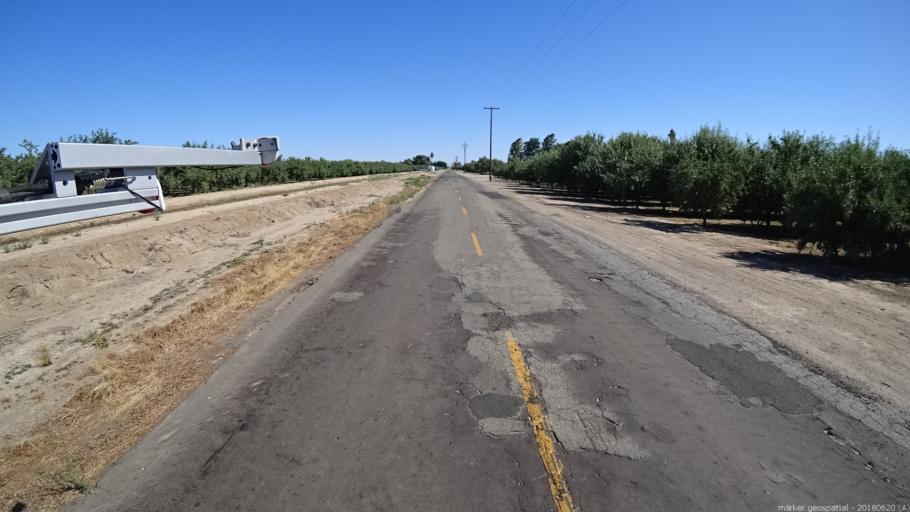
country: US
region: California
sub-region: Madera County
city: Parkwood
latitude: 36.8898
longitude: -120.0376
